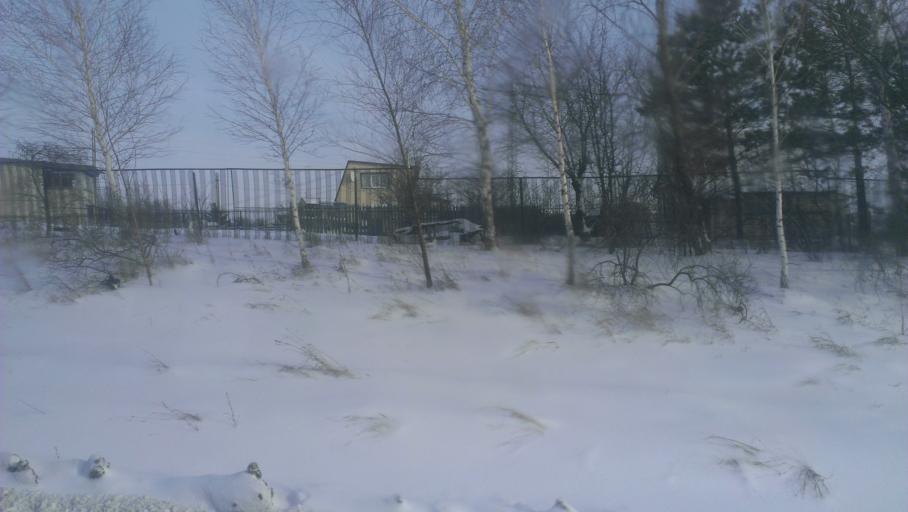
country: RU
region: Altai Krai
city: Gon'ba
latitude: 53.4166
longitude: 83.5499
